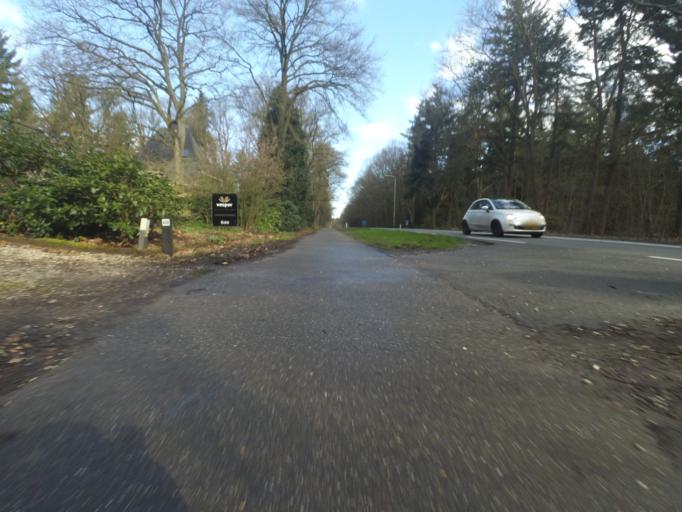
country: NL
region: Gelderland
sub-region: Gemeente Apeldoorn
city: Beekbergen
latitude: 52.1519
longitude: 5.9604
